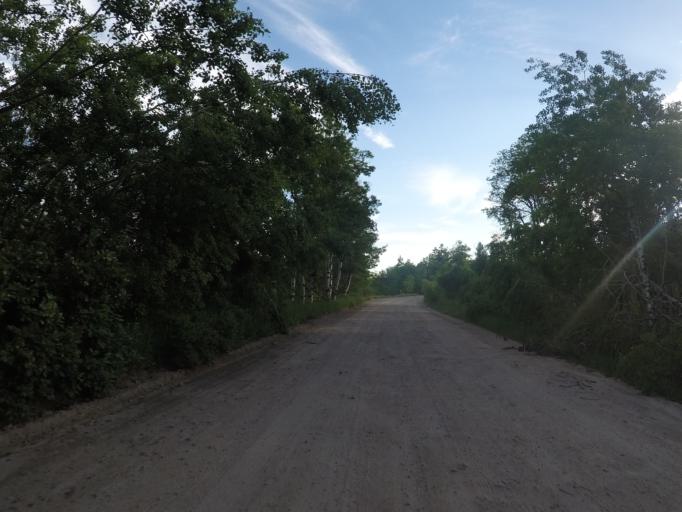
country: US
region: Montana
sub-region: Stillwater County
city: Absarokee
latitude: 45.2622
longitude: -109.5645
